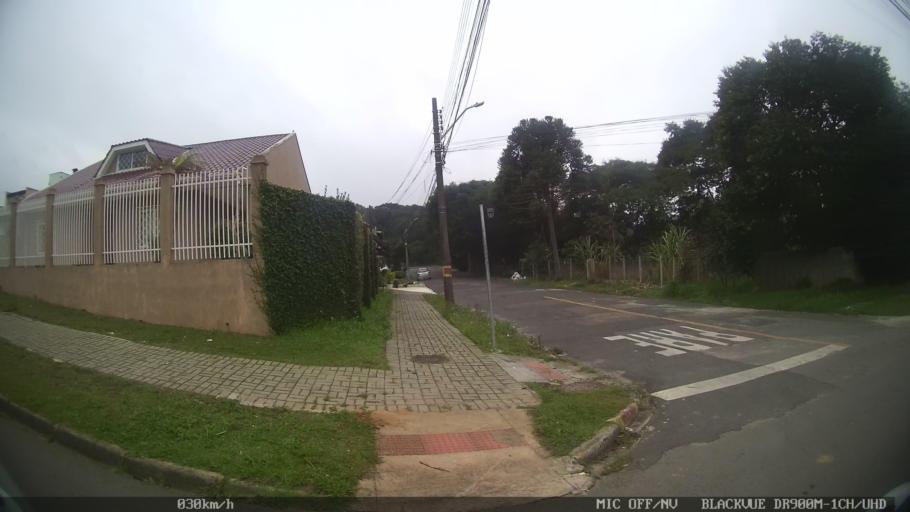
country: BR
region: Parana
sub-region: Almirante Tamandare
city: Almirante Tamandare
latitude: -25.3747
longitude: -49.3277
